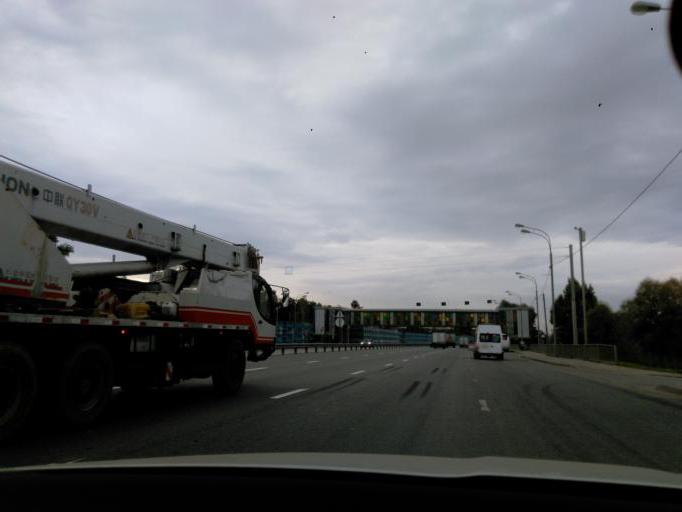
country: RU
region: Moscow
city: Severnyy
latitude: 55.9442
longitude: 37.5425
